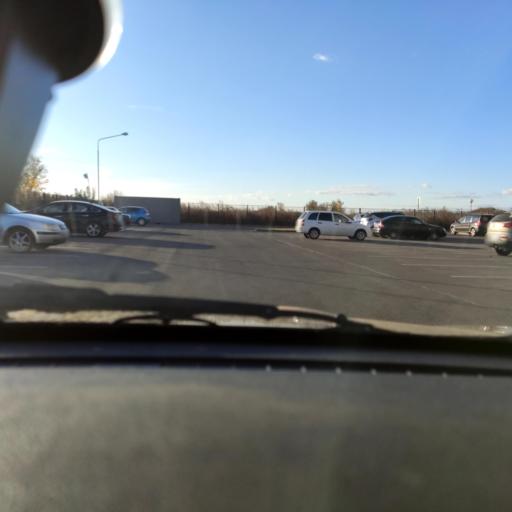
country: RU
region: Samara
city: Tol'yatti
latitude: 53.5176
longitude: 49.2561
